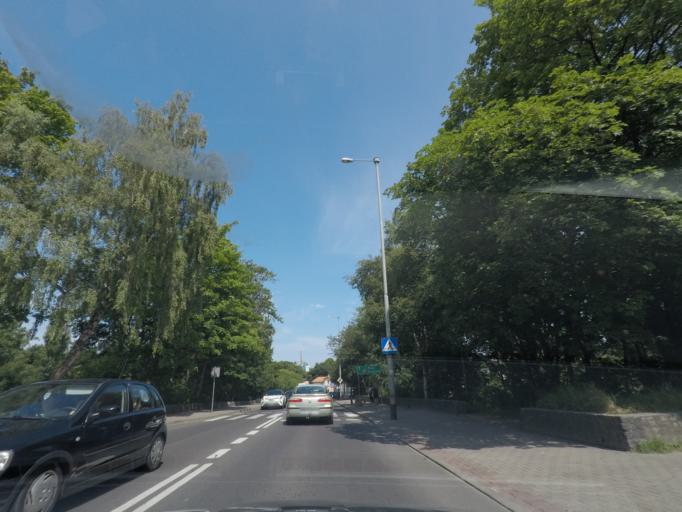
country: PL
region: Pomeranian Voivodeship
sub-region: Powiat slupski
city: Ustka
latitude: 54.5796
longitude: 16.8607
